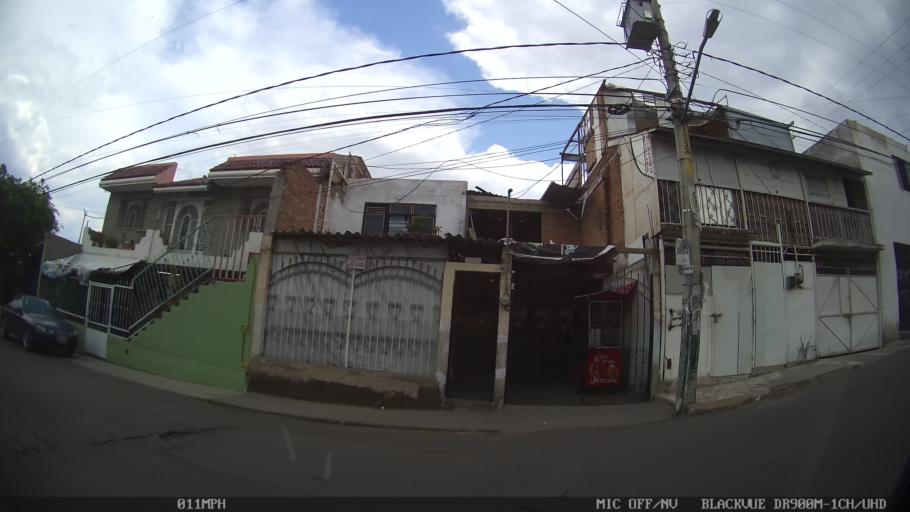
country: MX
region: Jalisco
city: Tlaquepaque
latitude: 20.6294
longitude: -103.2716
